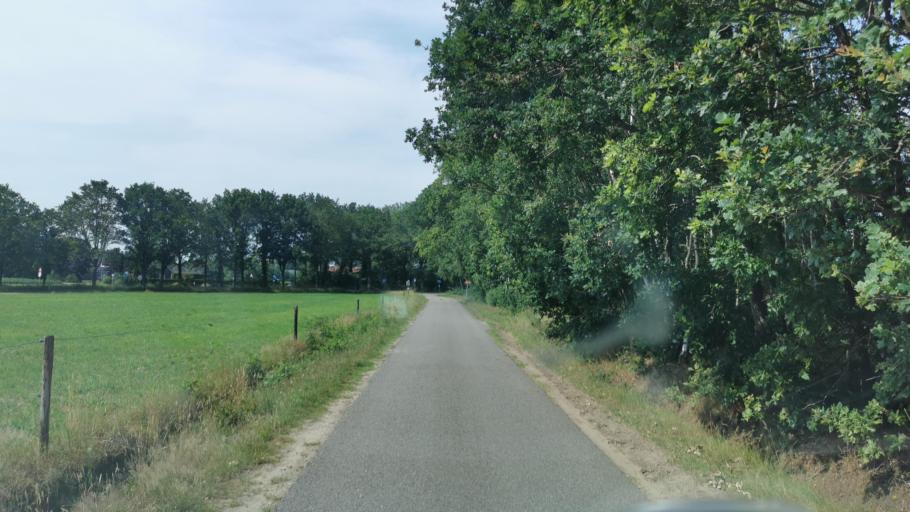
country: NL
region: Overijssel
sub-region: Gemeente Oldenzaal
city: Oldenzaal
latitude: 52.3093
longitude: 6.8621
